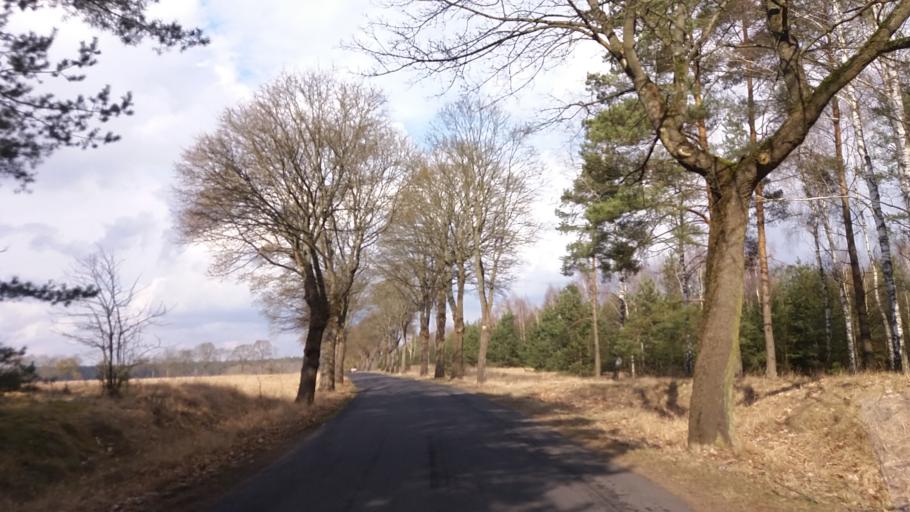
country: PL
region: West Pomeranian Voivodeship
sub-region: Powiat choszczenski
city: Drawno
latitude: 53.1670
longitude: 15.6854
